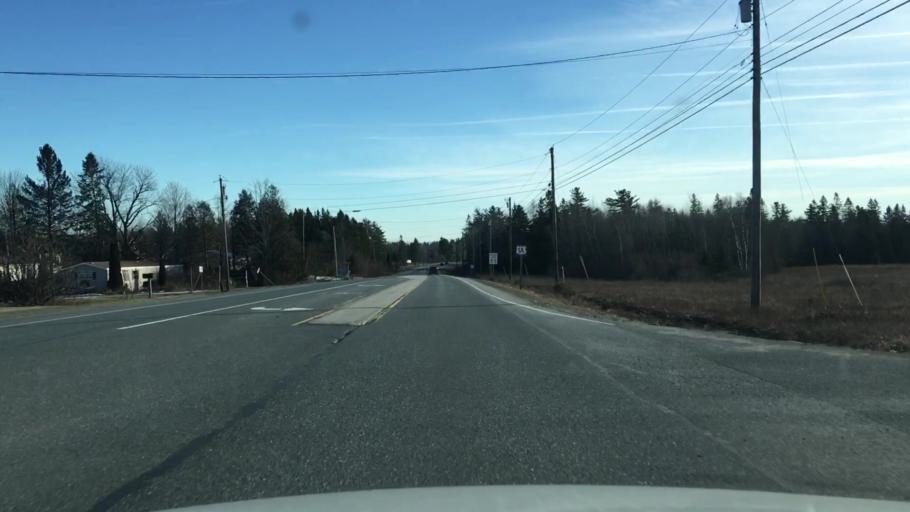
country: US
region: Maine
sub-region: Hancock County
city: Surry
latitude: 44.6156
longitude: -68.5252
